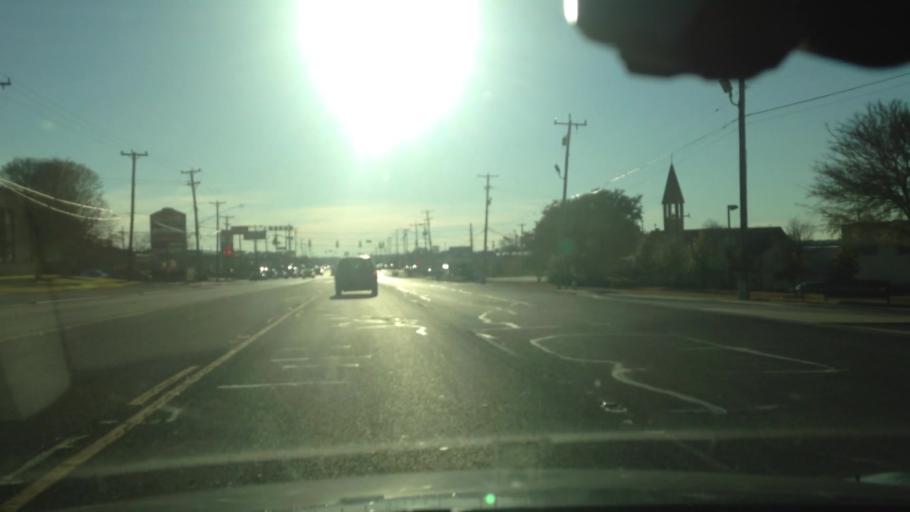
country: US
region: Texas
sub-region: Bexar County
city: Windcrest
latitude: 29.5113
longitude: -98.4066
